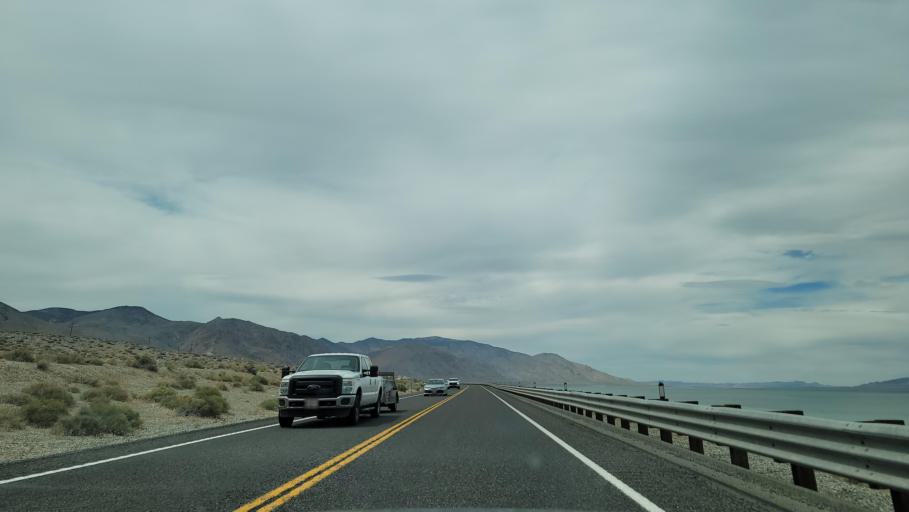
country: US
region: Nevada
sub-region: Mineral County
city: Hawthorne
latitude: 38.6038
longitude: -118.7109
